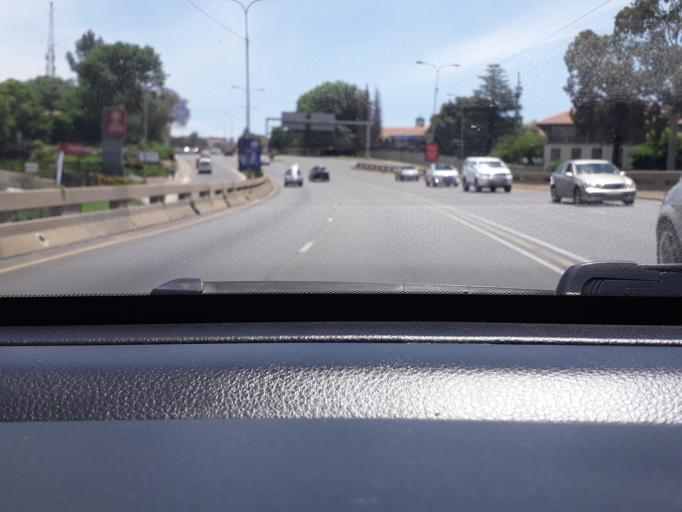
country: ZA
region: Gauteng
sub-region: City of Johannesburg Metropolitan Municipality
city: Modderfontein
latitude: -26.1023
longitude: 28.0701
